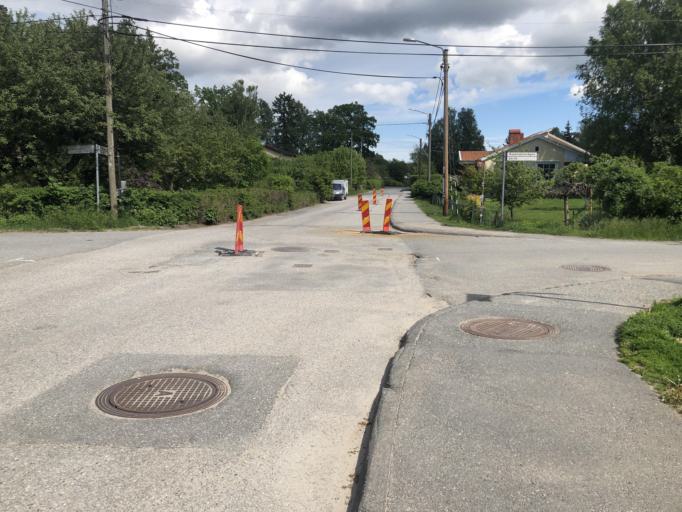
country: SE
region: Stockholm
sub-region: Huddinge Kommun
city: Huddinge
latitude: 59.2499
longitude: 17.9778
